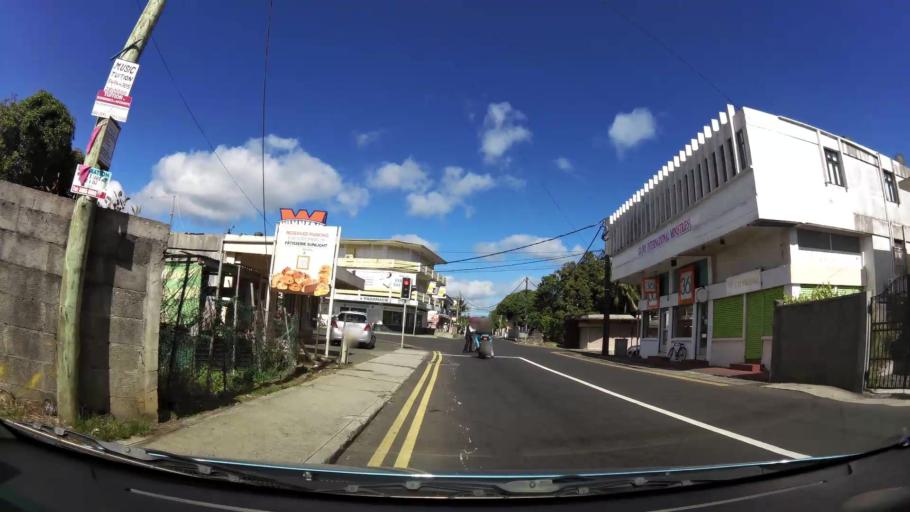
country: MU
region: Plaines Wilhems
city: Vacoas
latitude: -20.3054
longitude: 57.4921
